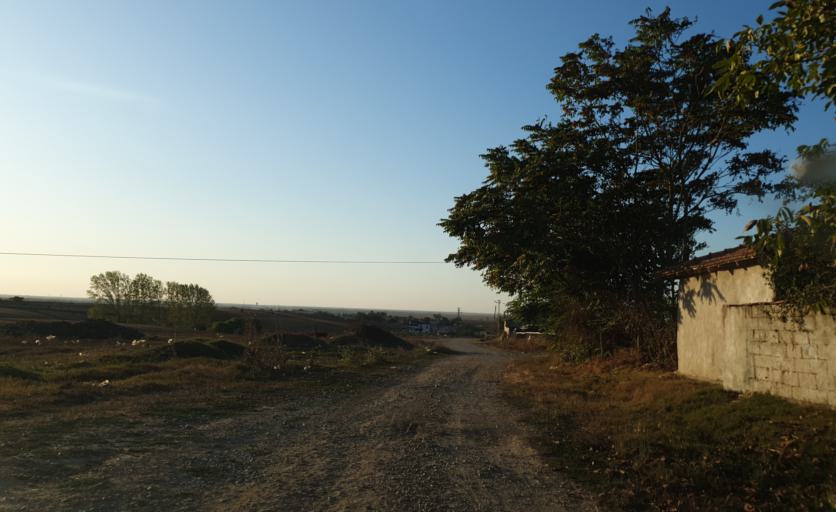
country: TR
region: Tekirdag
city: Beyazkoy
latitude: 41.3304
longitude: 27.7440
